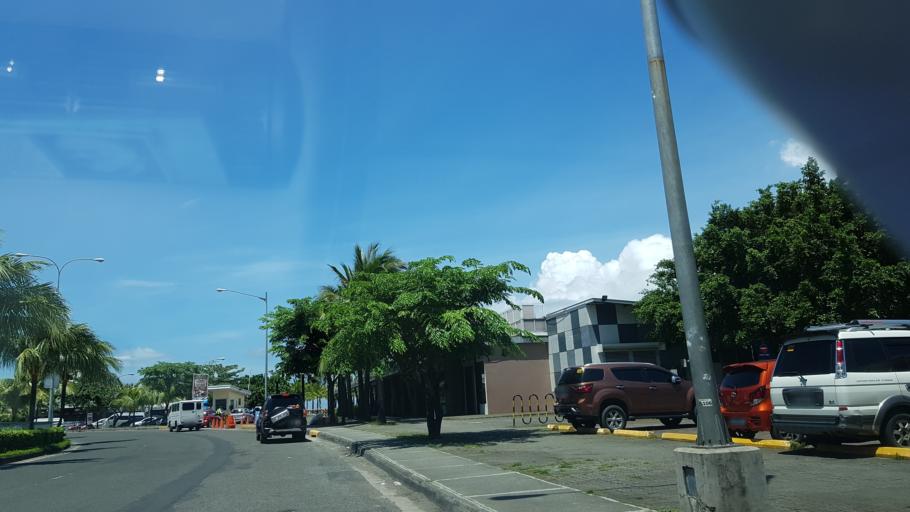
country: PH
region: Metro Manila
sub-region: City of Manila
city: Port Area
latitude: 14.5416
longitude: 120.9806
